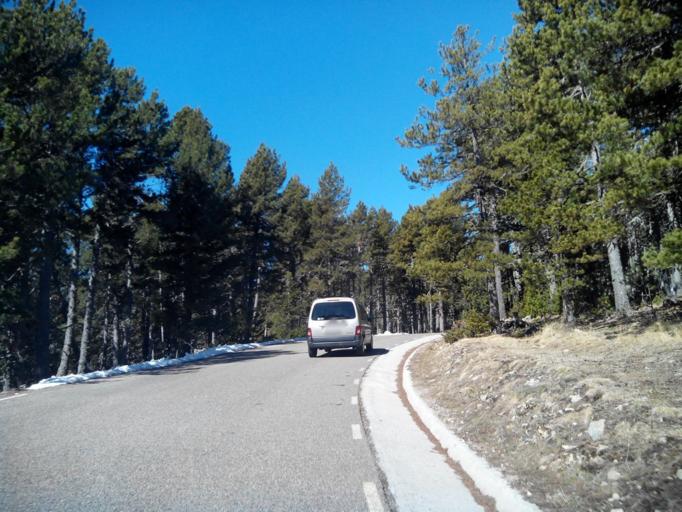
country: ES
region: Catalonia
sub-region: Provincia de Lleida
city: Lles de Cerdanya
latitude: 42.4242
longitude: 1.6652
